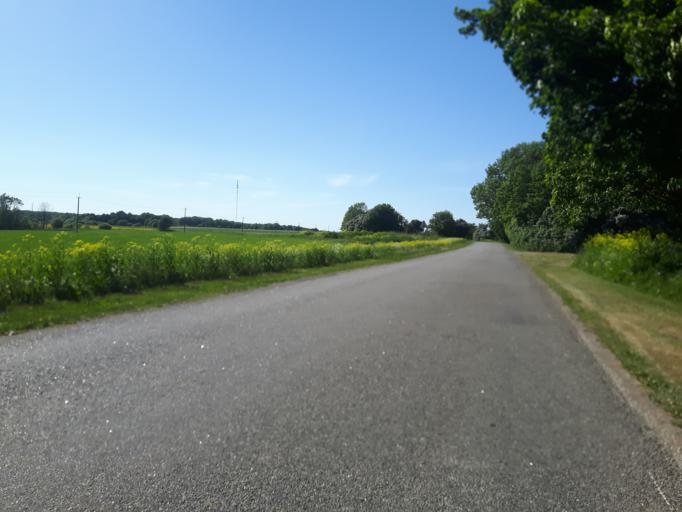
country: EE
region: Laeaene-Virumaa
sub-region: Haljala vald
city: Haljala
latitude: 59.5435
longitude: 26.1473
